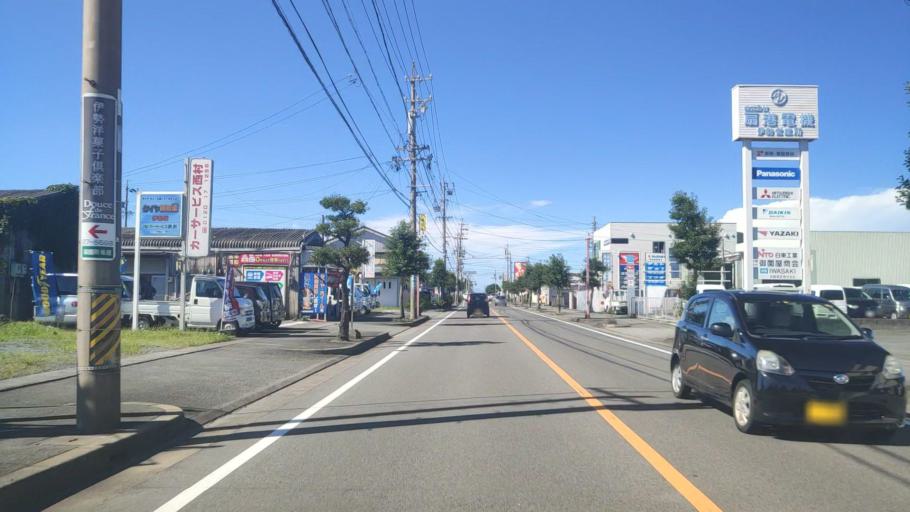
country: JP
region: Mie
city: Ise
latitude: 34.5052
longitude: 136.7083
